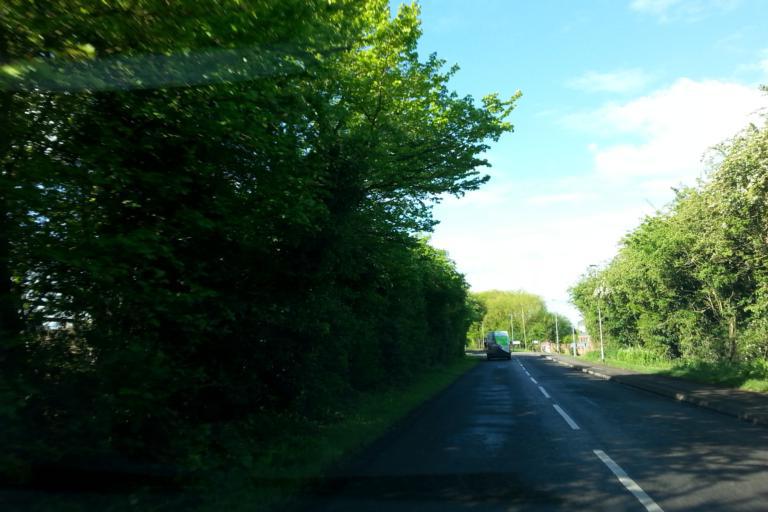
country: GB
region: England
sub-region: Nottinghamshire
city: Cotgrave
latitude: 52.9155
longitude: -1.0302
